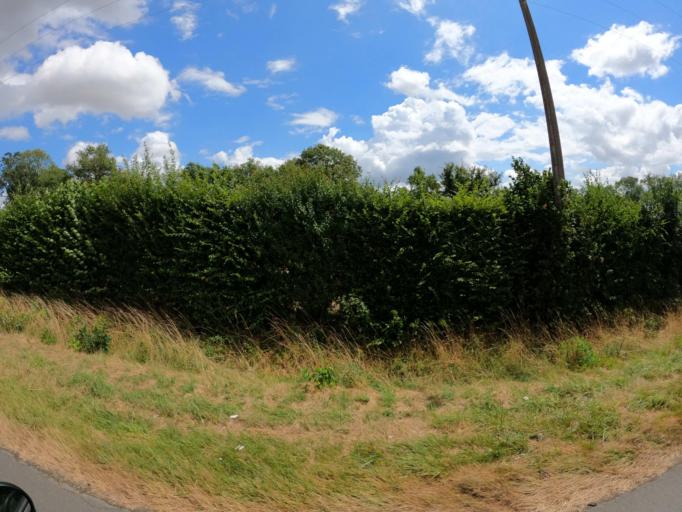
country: FR
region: Pays de la Loire
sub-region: Departement de Maine-et-Loire
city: Mire
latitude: 47.7640
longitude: -0.4841
